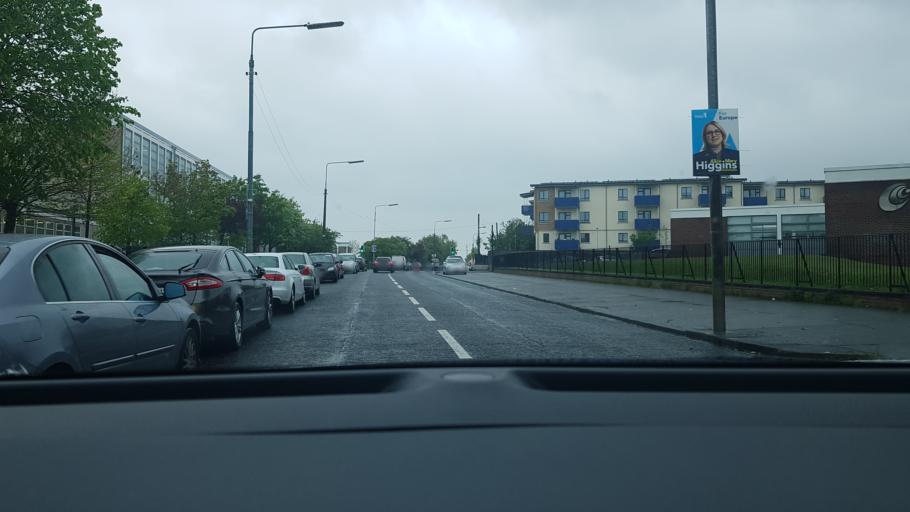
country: IE
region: Leinster
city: Chapelizod
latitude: 53.3442
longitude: -6.3499
